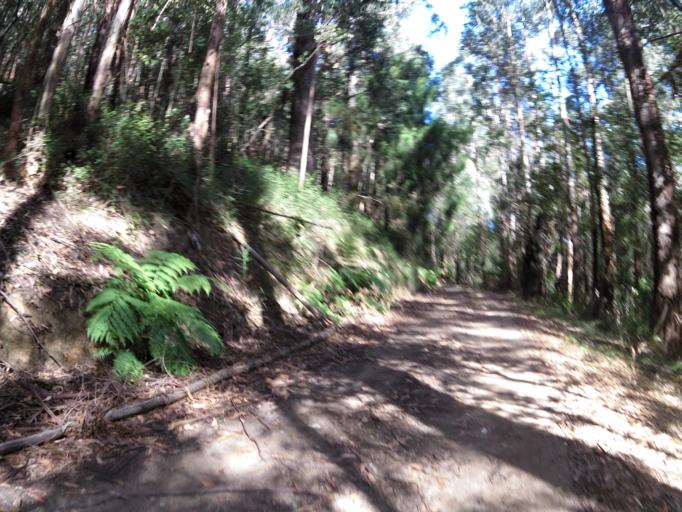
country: AU
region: Victoria
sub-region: Yarra Ranges
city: Millgrove
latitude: -37.8554
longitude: 145.7911
